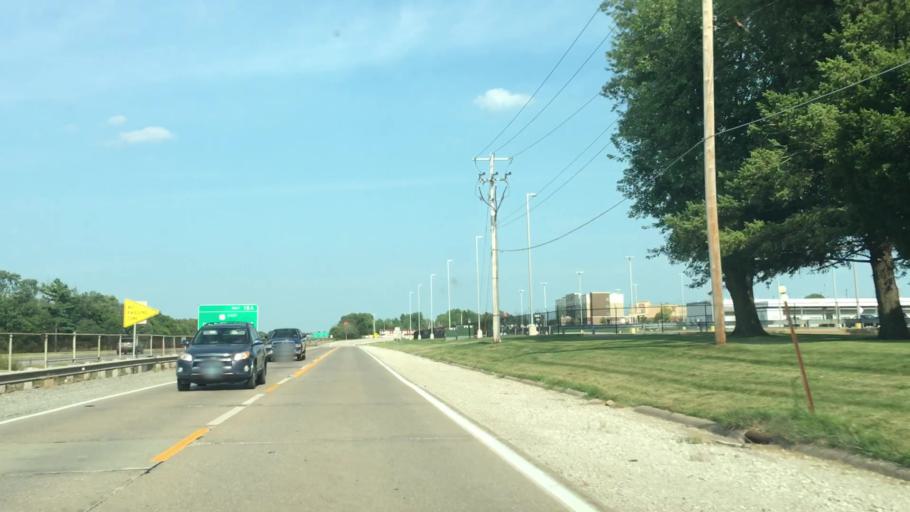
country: US
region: Illinois
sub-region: Rock Island County
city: Moline
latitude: 41.4576
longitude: -90.5097
